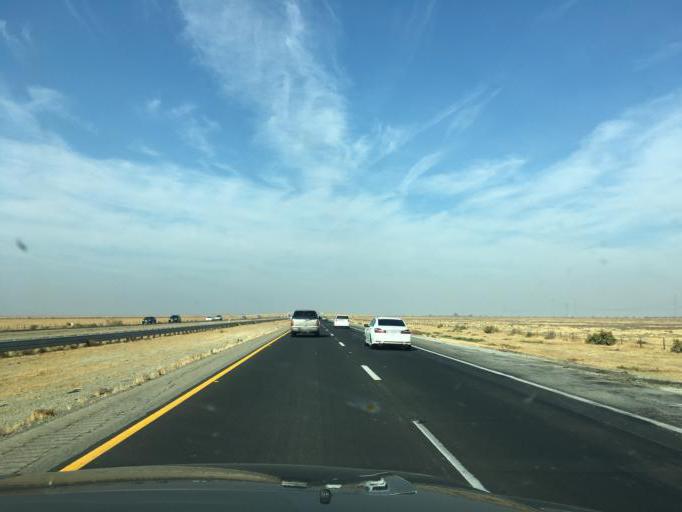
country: US
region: California
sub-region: Kings County
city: Kettleman City
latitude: 35.8359
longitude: -119.8169
